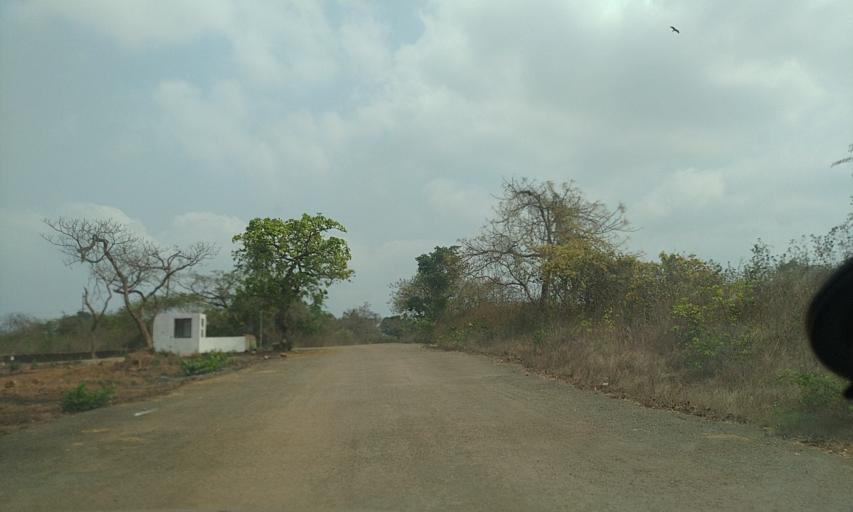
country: IN
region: Goa
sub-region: North Goa
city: Goa Velha
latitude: 15.4783
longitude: 73.9100
